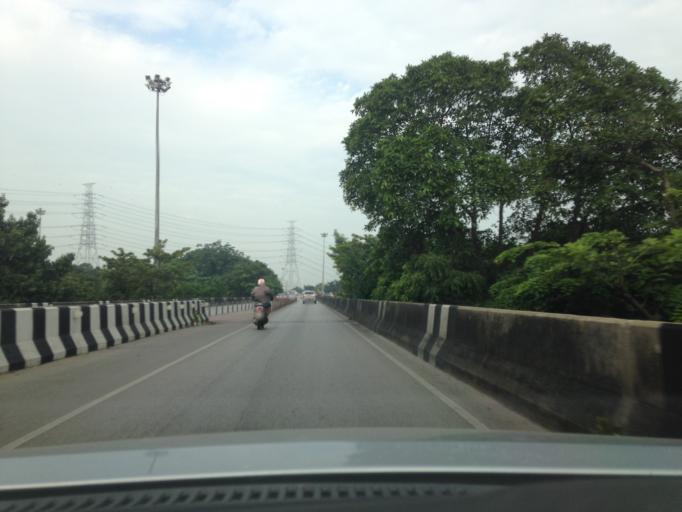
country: TH
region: Bangkok
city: Chatuchak
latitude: 13.8296
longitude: 100.5555
